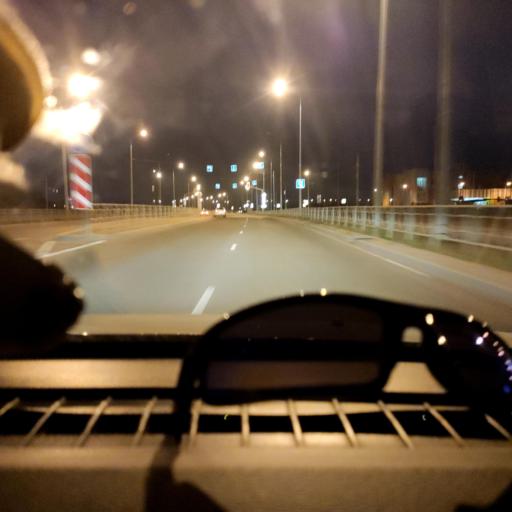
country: RU
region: Samara
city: Samara
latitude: 53.0993
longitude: 50.1636
